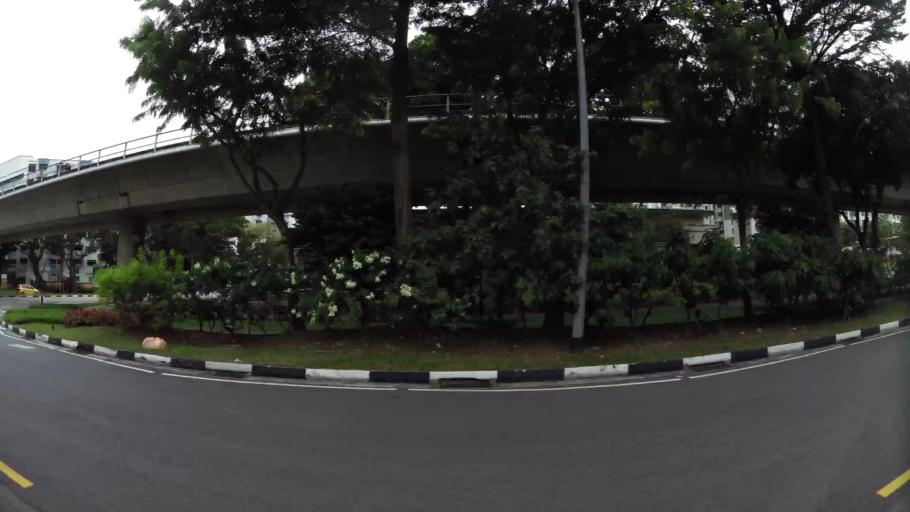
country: MY
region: Johor
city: Johor Bahru
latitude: 1.4391
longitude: 103.7952
